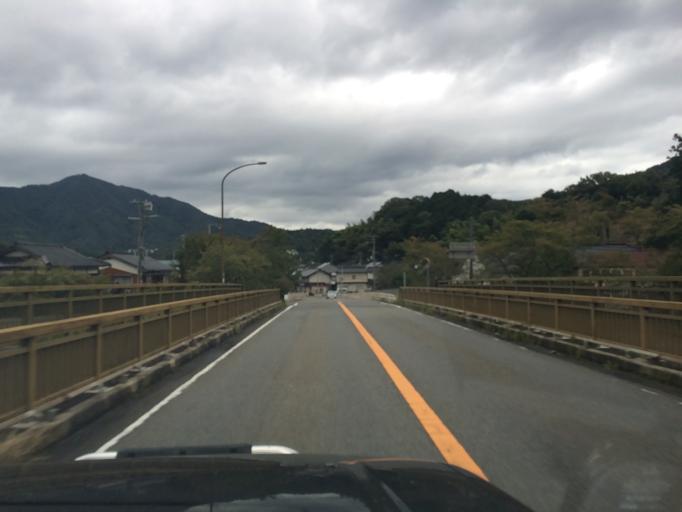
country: JP
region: Hyogo
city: Toyooka
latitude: 35.4277
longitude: 134.7937
